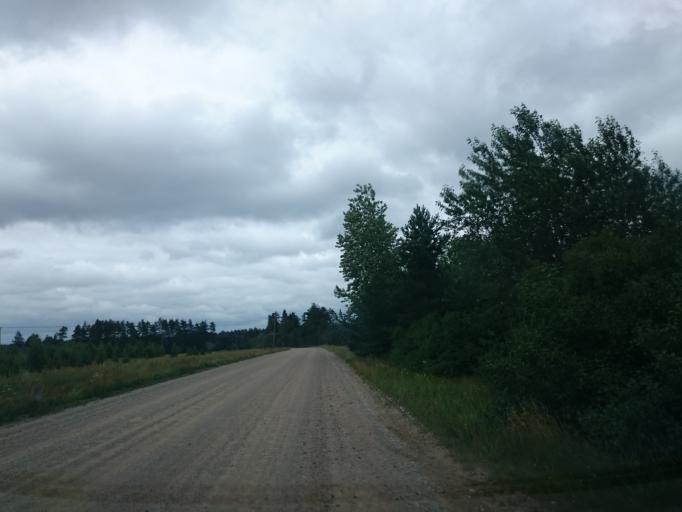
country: LV
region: Pavilostas
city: Pavilosta
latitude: 56.7639
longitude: 21.2751
